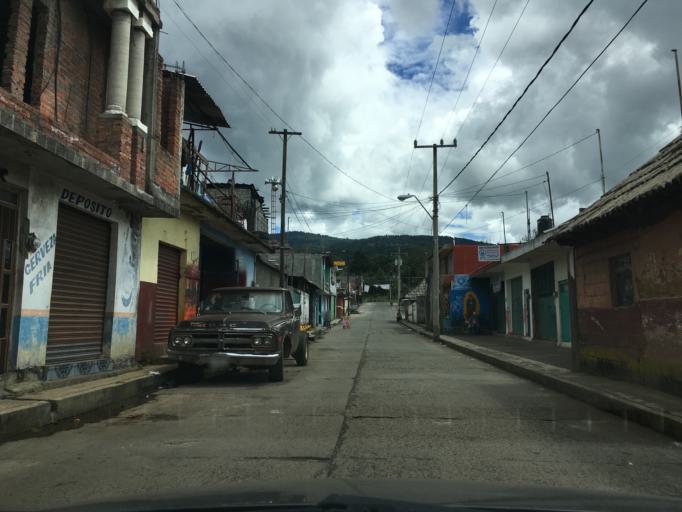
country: MX
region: Michoacan
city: Nahuatzen
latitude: 19.6535
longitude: -101.9144
